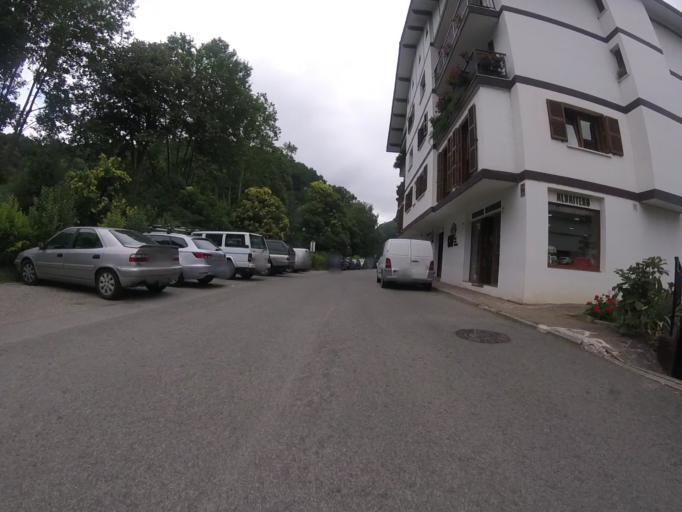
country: ES
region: Navarre
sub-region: Provincia de Navarra
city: Doneztebe
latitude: 43.1341
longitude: -1.6659
